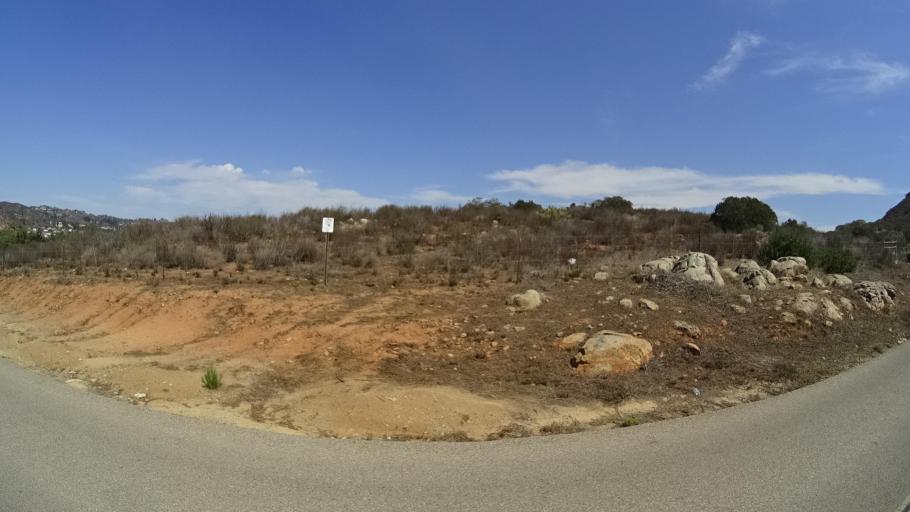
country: US
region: California
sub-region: San Diego County
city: Rancho San Diego
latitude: 32.7285
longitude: -116.9396
